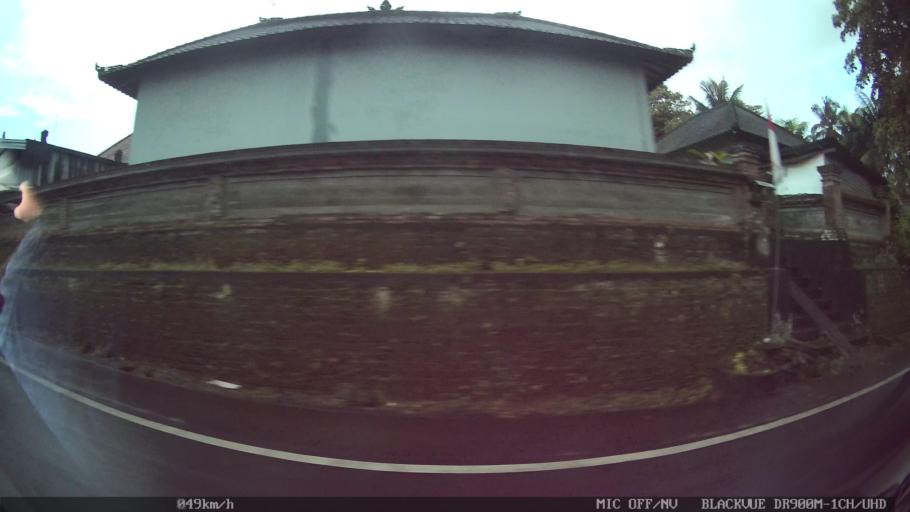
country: ID
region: Bali
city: Banjar Teguan
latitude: -8.5094
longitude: 115.2298
